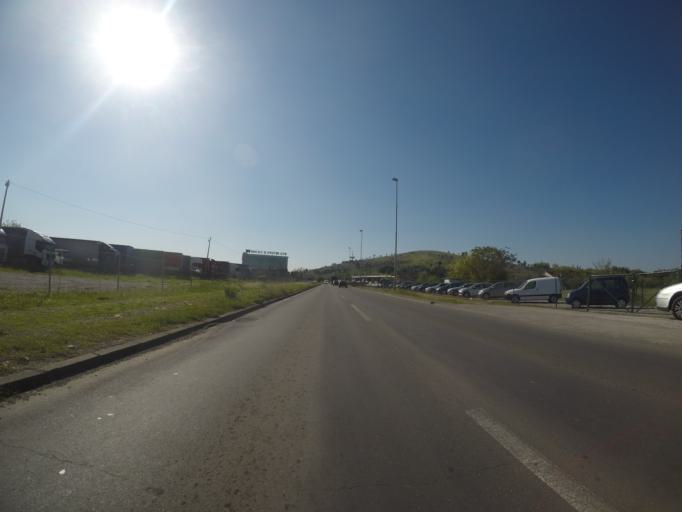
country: ME
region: Podgorica
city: Podgorica
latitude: 42.4279
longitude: 19.2330
